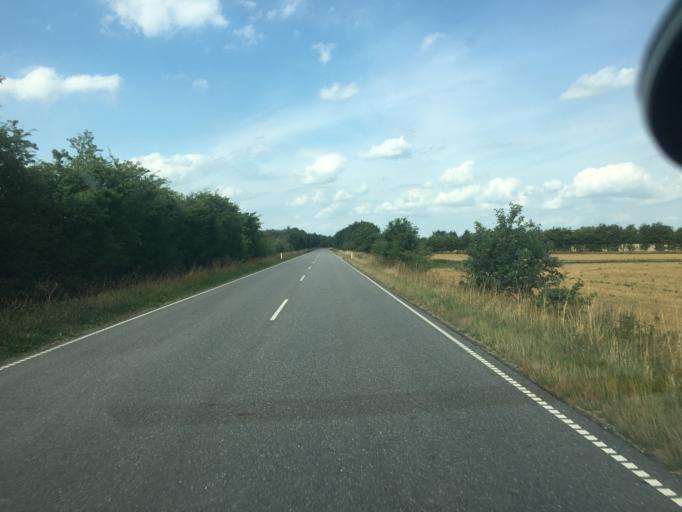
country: DK
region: South Denmark
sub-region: Aabenraa Kommune
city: Tinglev
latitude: 54.9387
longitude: 9.3059
